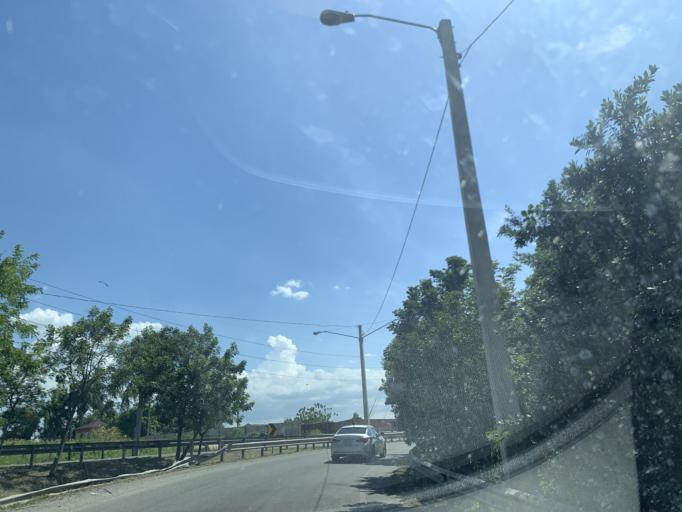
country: DO
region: Santiago
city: Palmar Arriba
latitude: 19.5162
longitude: -70.7631
